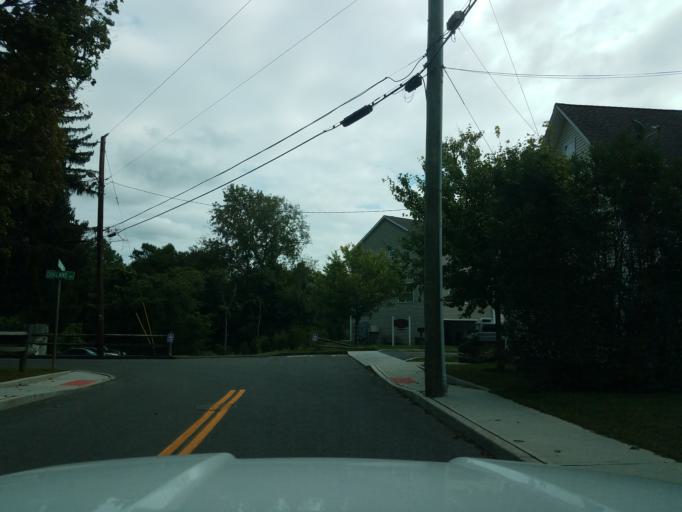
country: US
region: Connecticut
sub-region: Fairfield County
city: Danbury
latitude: 41.4086
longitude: -73.4534
